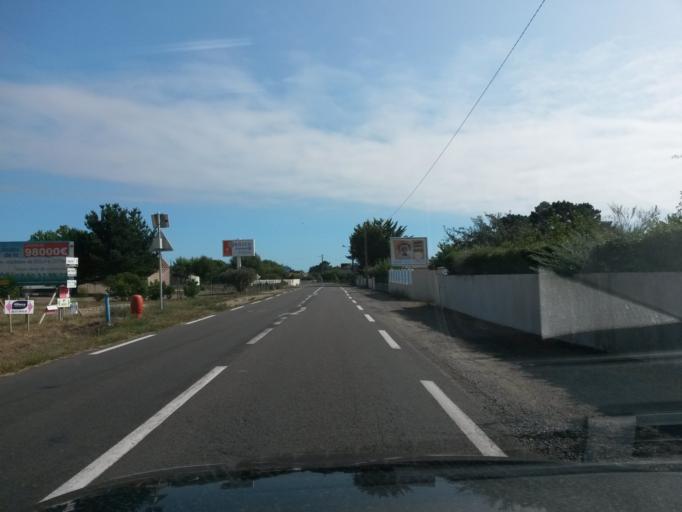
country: FR
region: Pays de la Loire
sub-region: Departement de la Vendee
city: Olonne-sur-Mer
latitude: 46.5559
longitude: -1.8110
